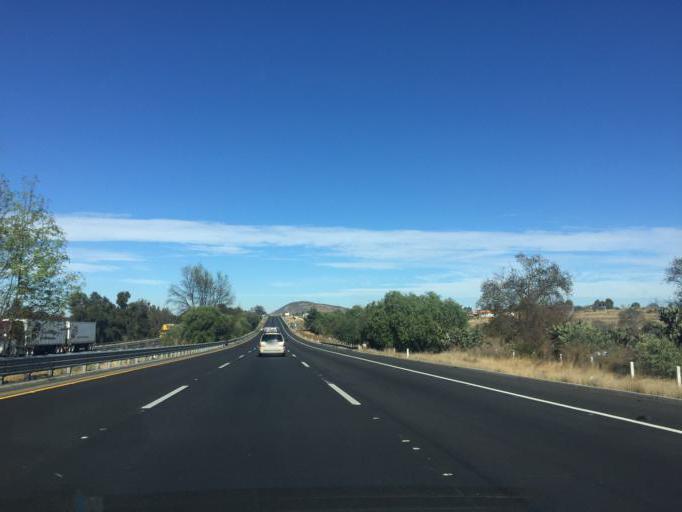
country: MX
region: Mexico
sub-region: Aculco
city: El Colorado
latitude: 20.1889
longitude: -99.7722
